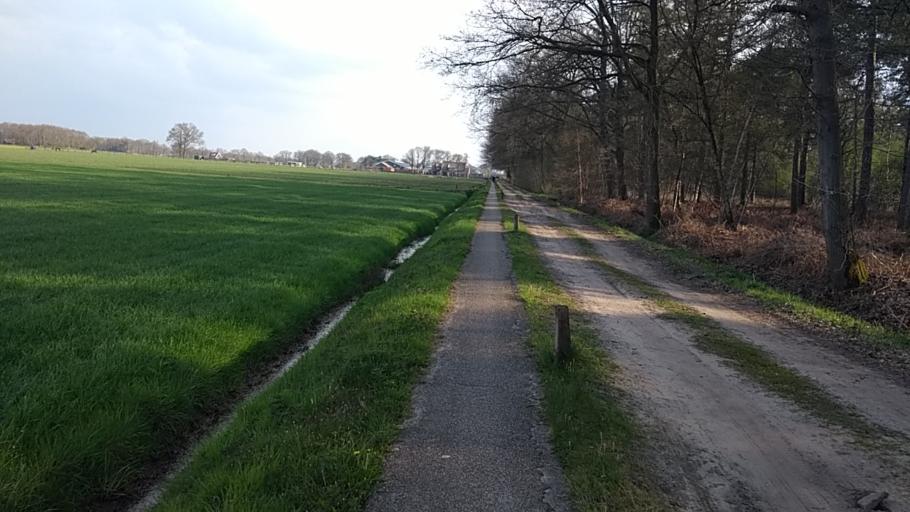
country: NL
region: Overijssel
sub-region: Gemeente Borne
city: Borne
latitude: 52.3553
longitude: 6.7267
